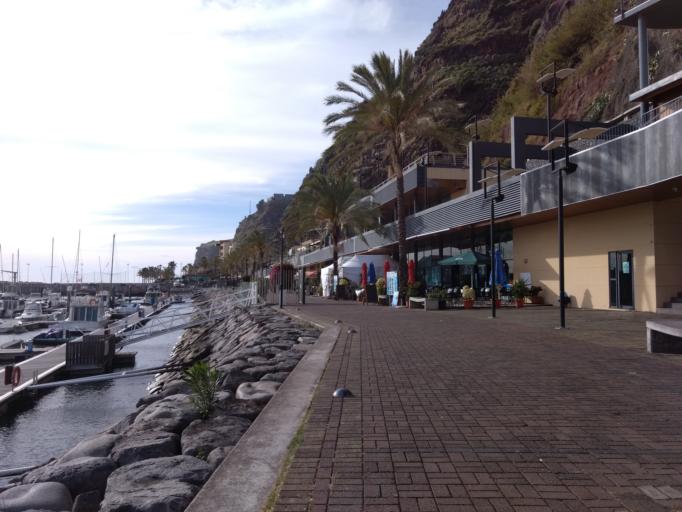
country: PT
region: Madeira
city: Calheta
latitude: 32.7181
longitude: -17.1709
